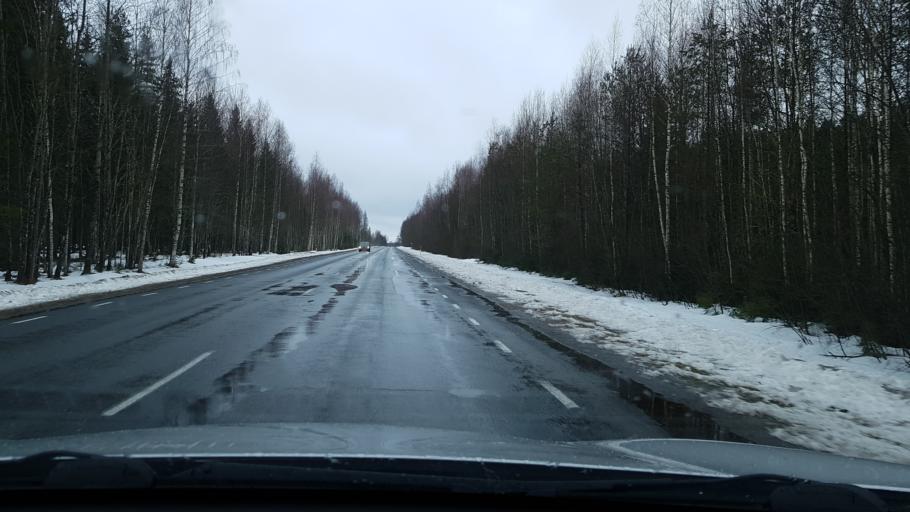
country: LV
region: Apes Novads
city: Ape
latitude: 57.7072
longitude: 26.7516
